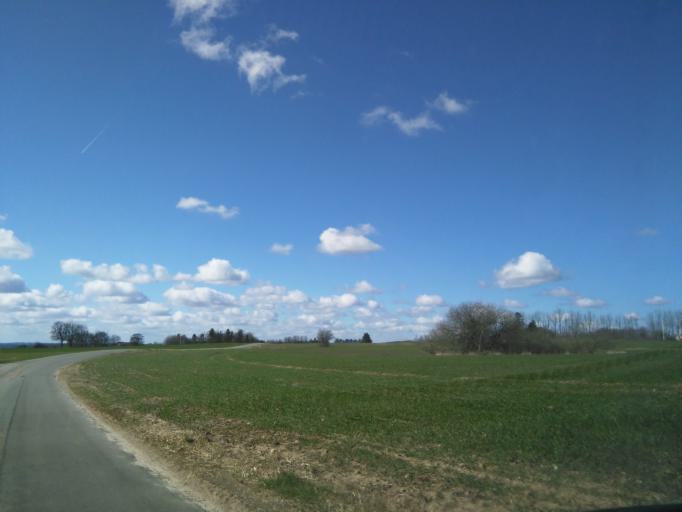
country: DK
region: Central Jutland
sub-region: Skanderborg Kommune
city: Skanderborg
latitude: 56.0748
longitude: 9.8721
